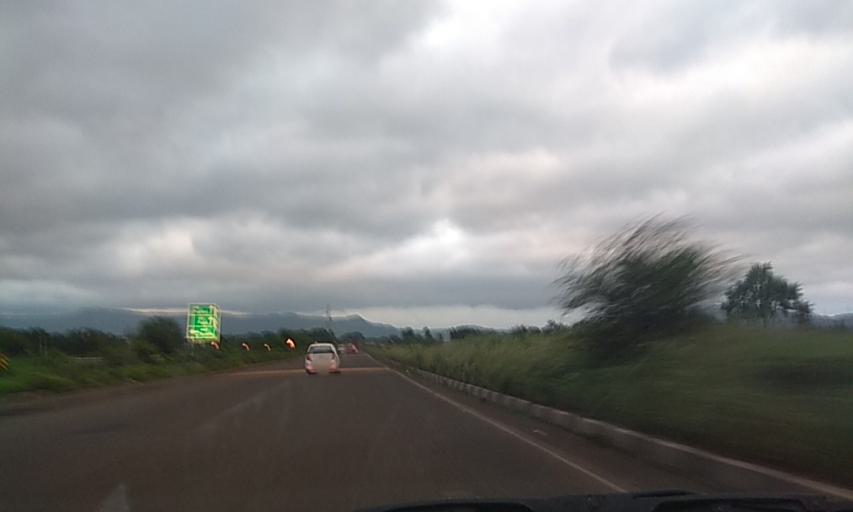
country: IN
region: Maharashtra
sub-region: Satara Division
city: Wai
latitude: 17.9397
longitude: 73.9772
